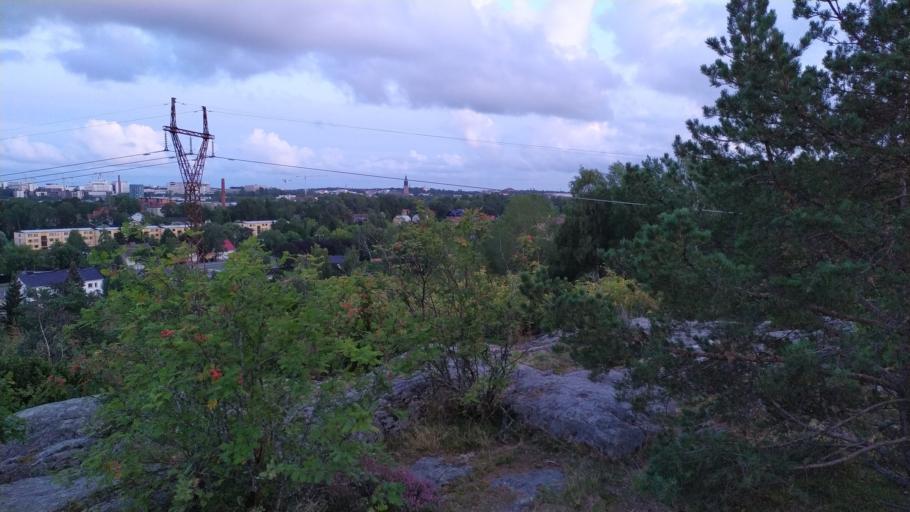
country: FI
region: Varsinais-Suomi
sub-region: Turku
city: Turku
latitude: 60.4715
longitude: 22.2771
